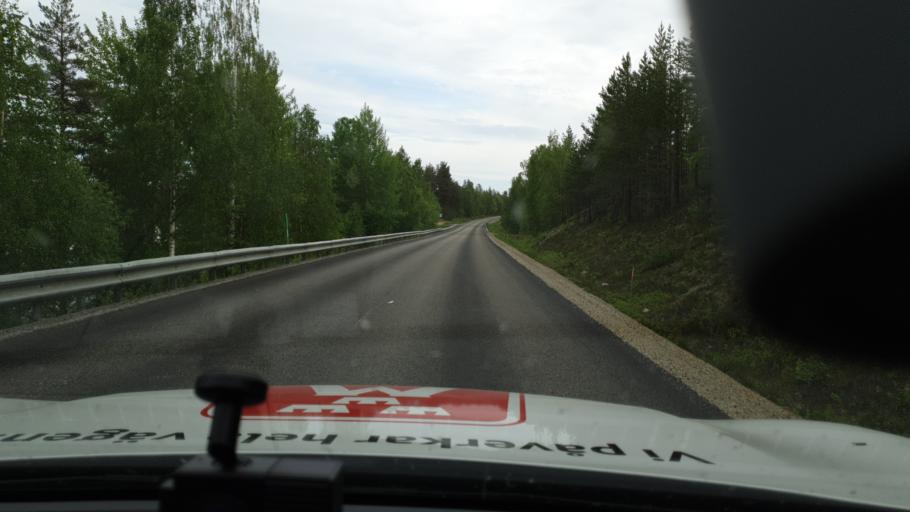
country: SE
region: Vaesterbotten
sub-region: Lycksele Kommun
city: Lycksele
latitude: 64.8660
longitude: 18.7211
